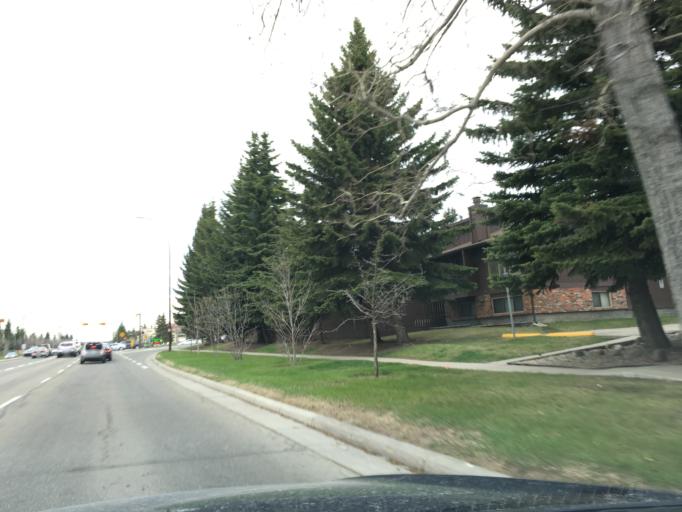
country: CA
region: Alberta
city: Calgary
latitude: 50.9614
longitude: -114.1163
